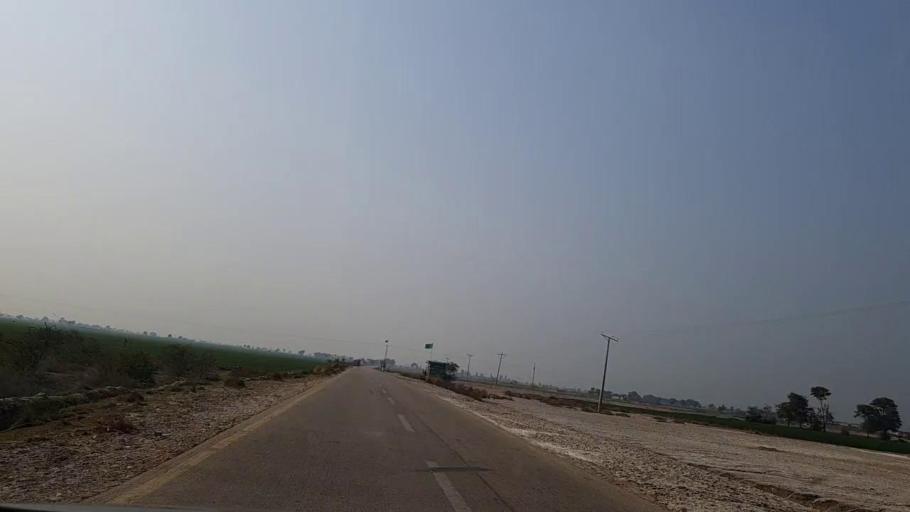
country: PK
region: Sindh
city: Sakrand
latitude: 26.1360
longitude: 68.1858
